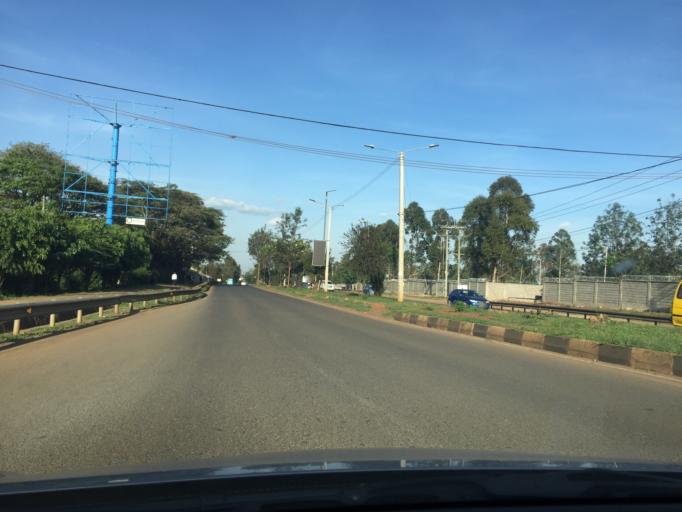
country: KE
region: Nairobi Area
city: Nairobi
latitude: -1.3326
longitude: 36.7819
